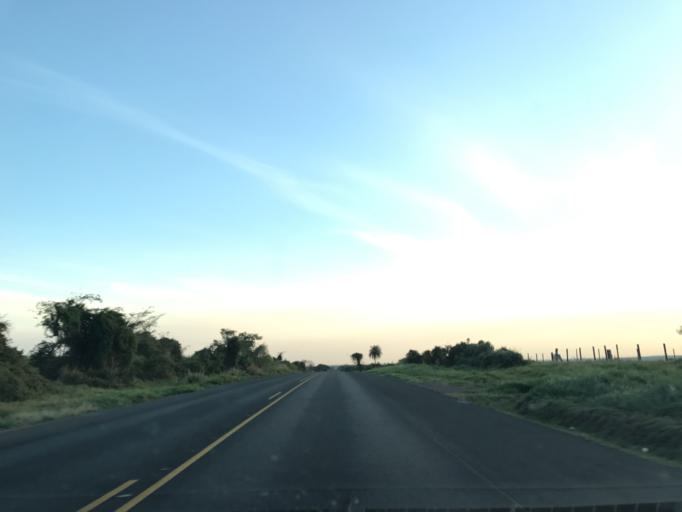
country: BR
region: Sao Paulo
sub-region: Pirapozinho
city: Pirapozinho
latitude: -22.4047
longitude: -51.6257
